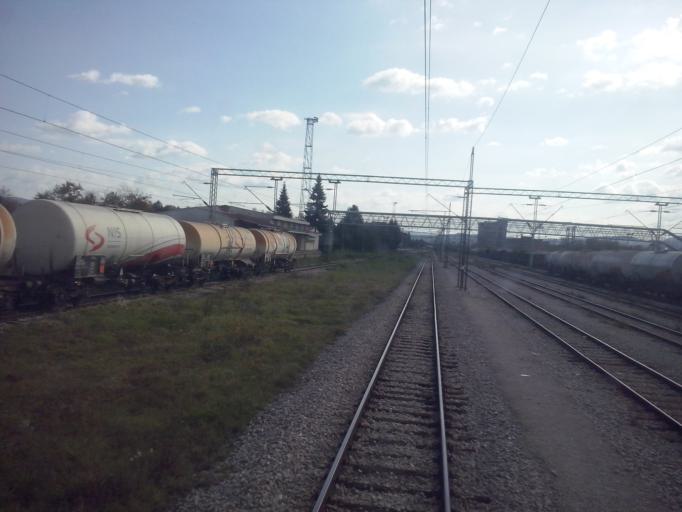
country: RS
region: Central Serbia
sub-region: Zlatiborski Okrug
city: Pozega
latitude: 43.8445
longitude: 20.0241
